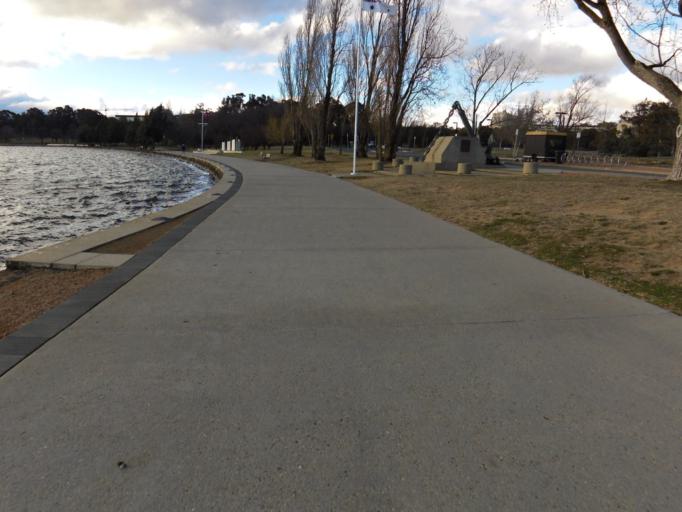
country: AU
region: Australian Capital Territory
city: Canberra
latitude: -35.2981
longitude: 149.1433
